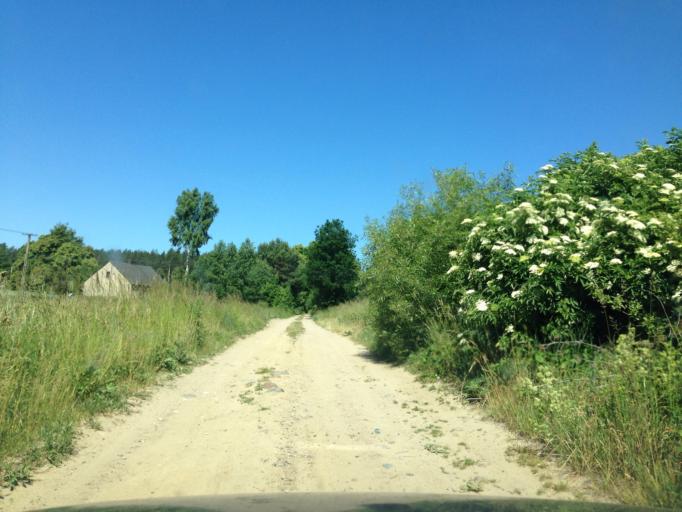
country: PL
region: Kujawsko-Pomorskie
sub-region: Powiat brodnicki
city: Bartniczka
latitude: 53.2618
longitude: 19.5848
